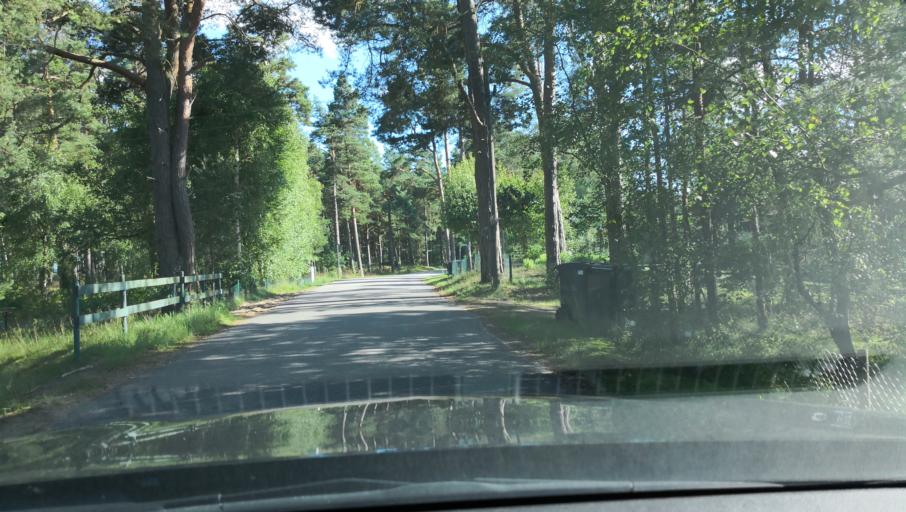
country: SE
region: Skane
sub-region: Simrishamns Kommun
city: Kivik
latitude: 55.7761
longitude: 14.1972
